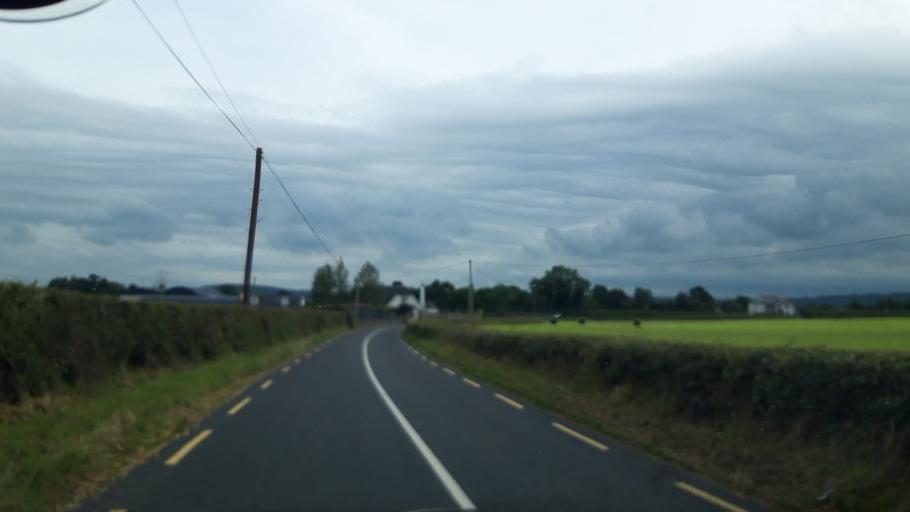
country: IE
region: Leinster
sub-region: Kilkenny
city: Ballyragget
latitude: 52.7503
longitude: -7.3906
